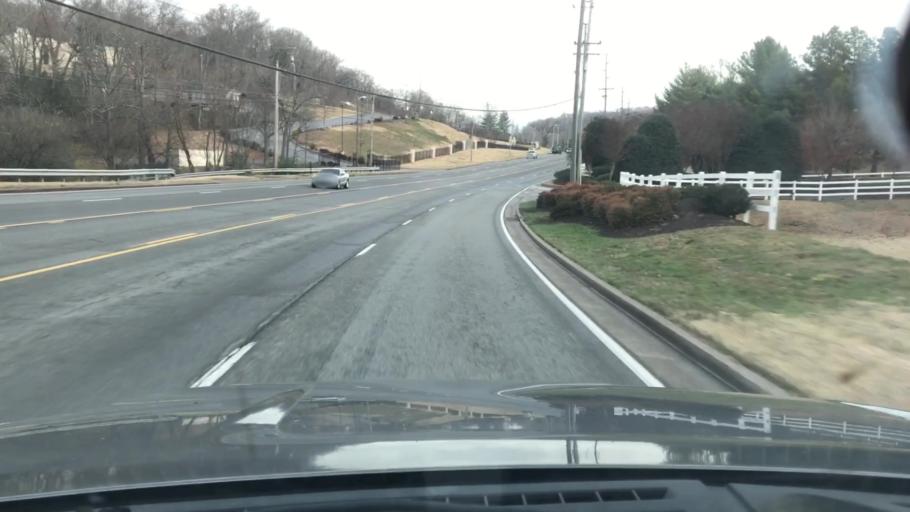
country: US
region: Tennessee
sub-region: Davidson County
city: Belle Meade
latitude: 36.0990
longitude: -86.9246
